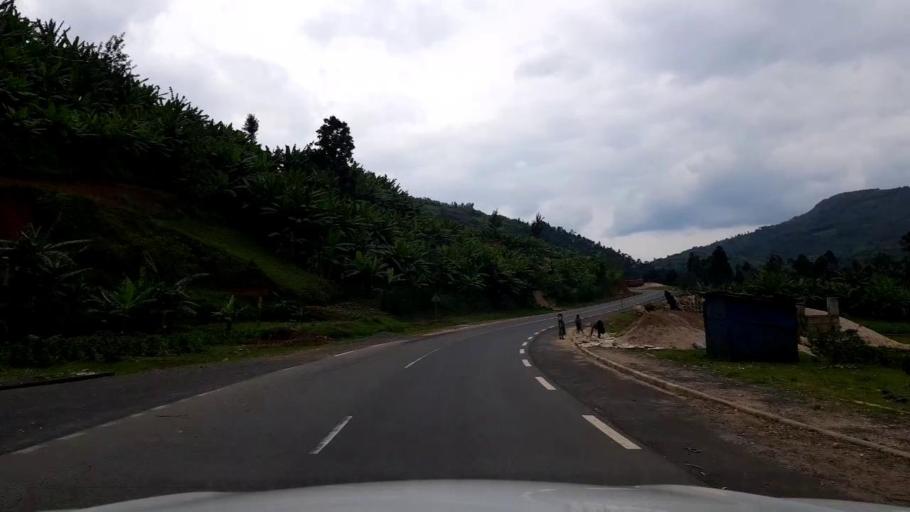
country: RW
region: Western Province
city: Kibuye
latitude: -1.9162
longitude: 29.3691
